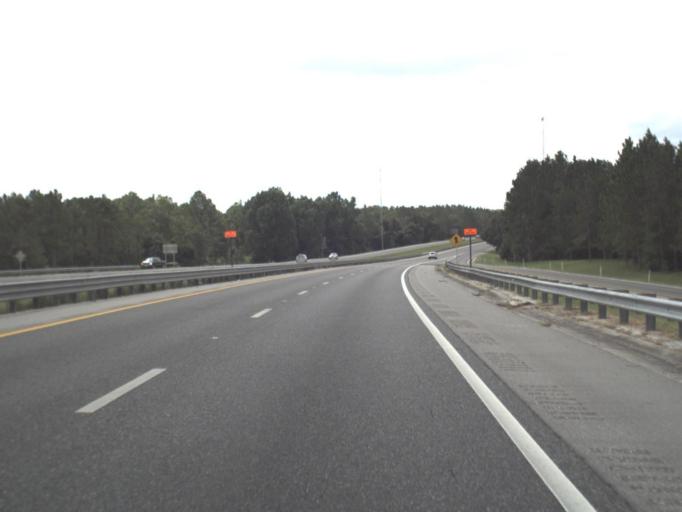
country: US
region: Florida
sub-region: Hernando County
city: Hill 'n Dale
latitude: 28.5220
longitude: -82.2372
